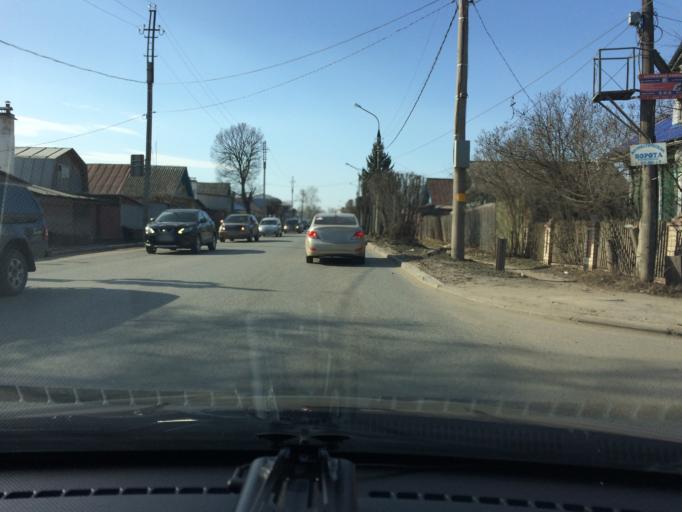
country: RU
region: Mariy-El
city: Yoshkar-Ola
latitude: 56.6465
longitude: 47.9069
